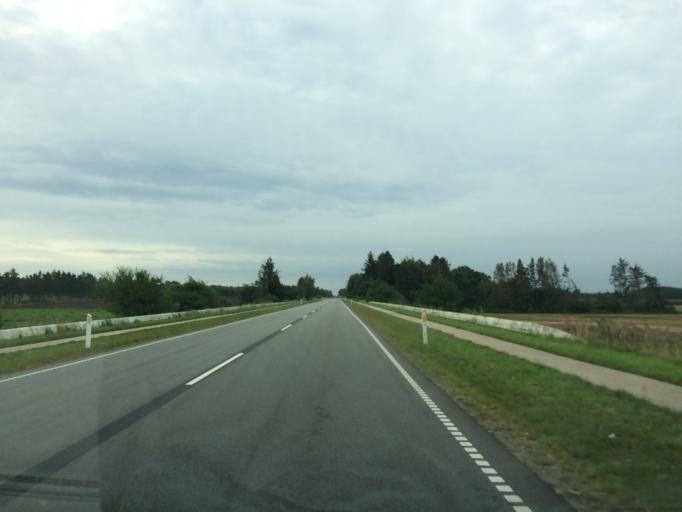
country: DK
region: Central Jutland
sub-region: Herning Kommune
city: Lind
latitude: 56.0750
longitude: 8.9865
